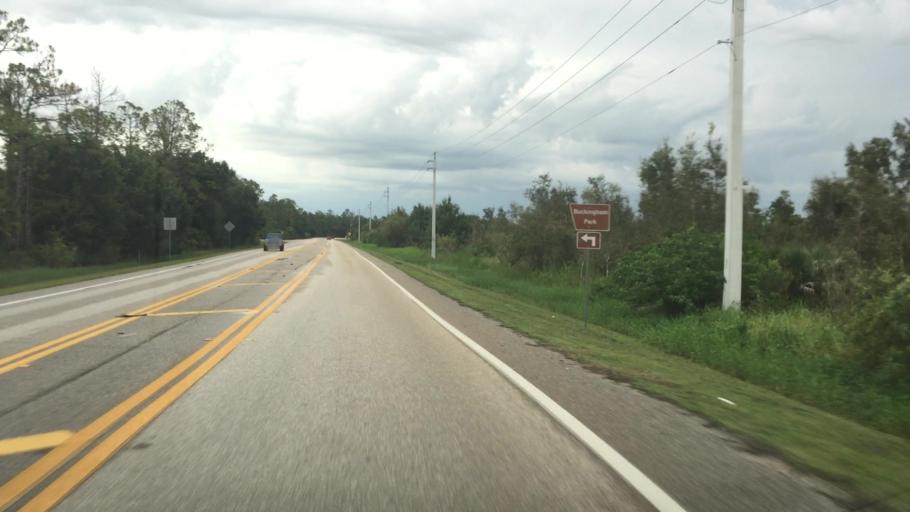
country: US
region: Florida
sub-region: Lee County
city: Gateway
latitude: 26.6290
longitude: -81.7569
